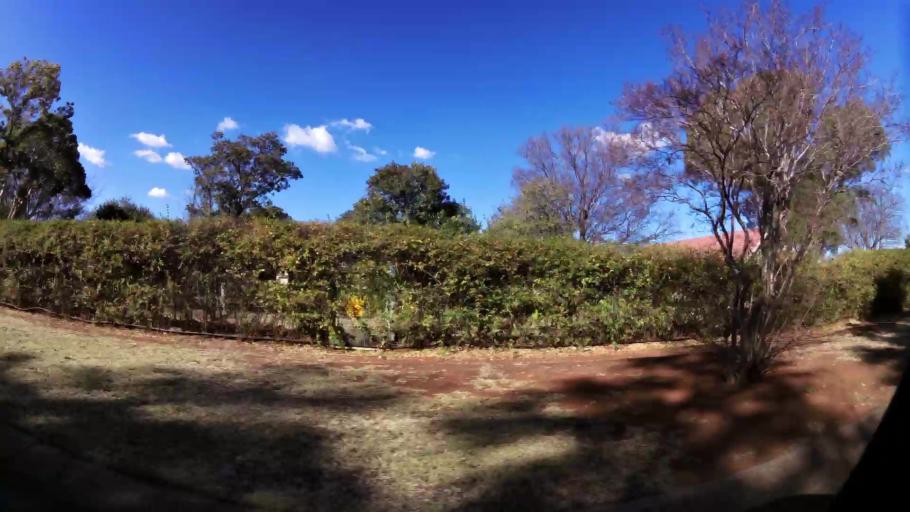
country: ZA
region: Gauteng
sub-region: West Rand District Municipality
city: Carletonville
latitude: -26.3717
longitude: 27.4095
